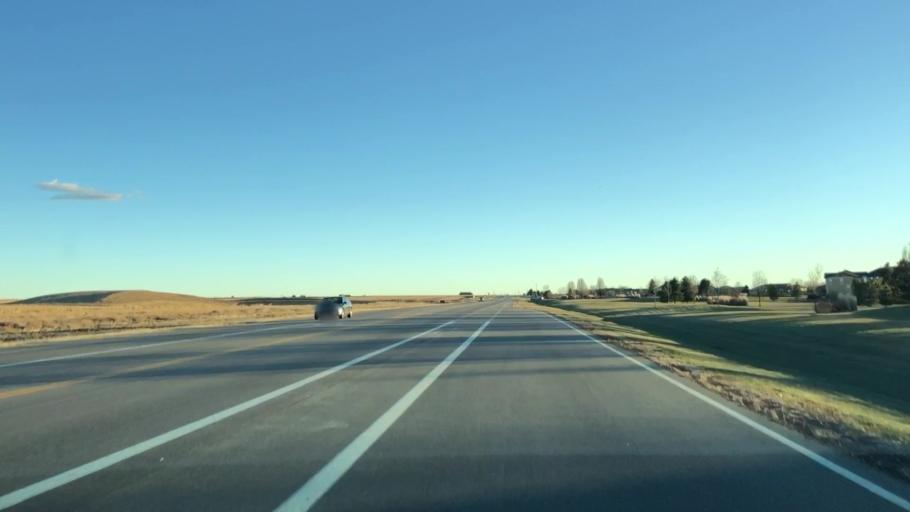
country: US
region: Colorado
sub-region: Weld County
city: Windsor
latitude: 40.4540
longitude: -104.9442
